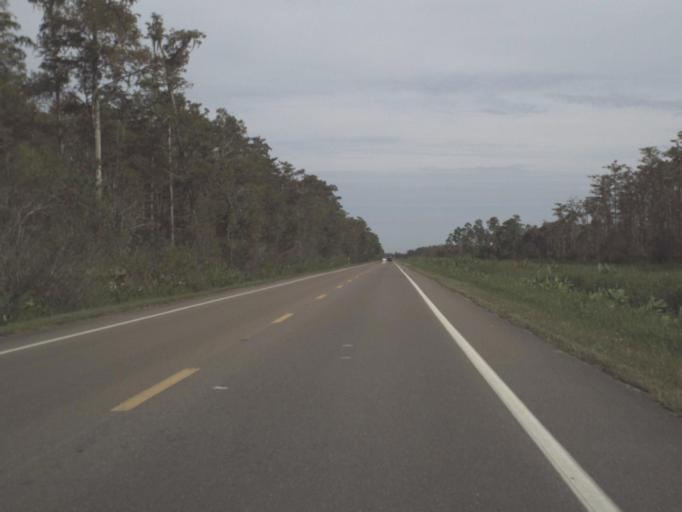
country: US
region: Florida
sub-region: Lee County
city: Olga
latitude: 26.9267
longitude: -81.7606
